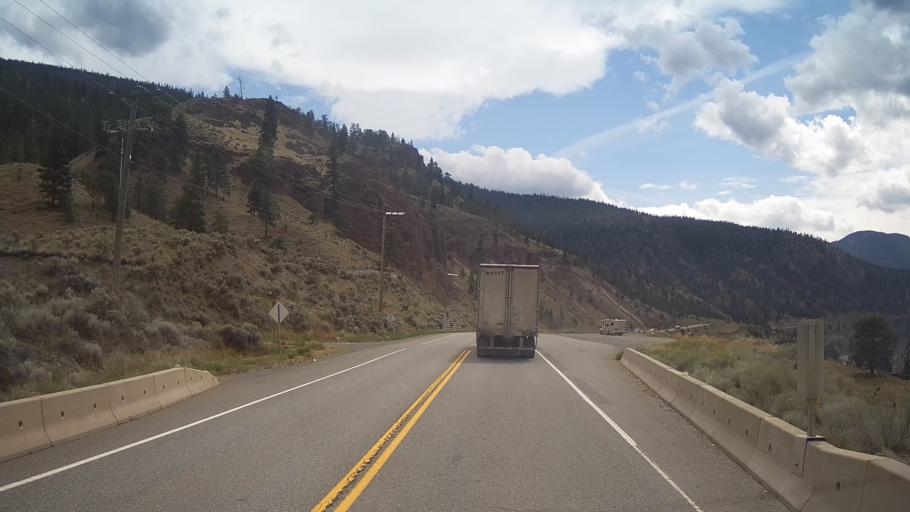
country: CA
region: British Columbia
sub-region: Thompson-Nicola Regional District
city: Ashcroft
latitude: 50.3108
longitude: -121.3954
